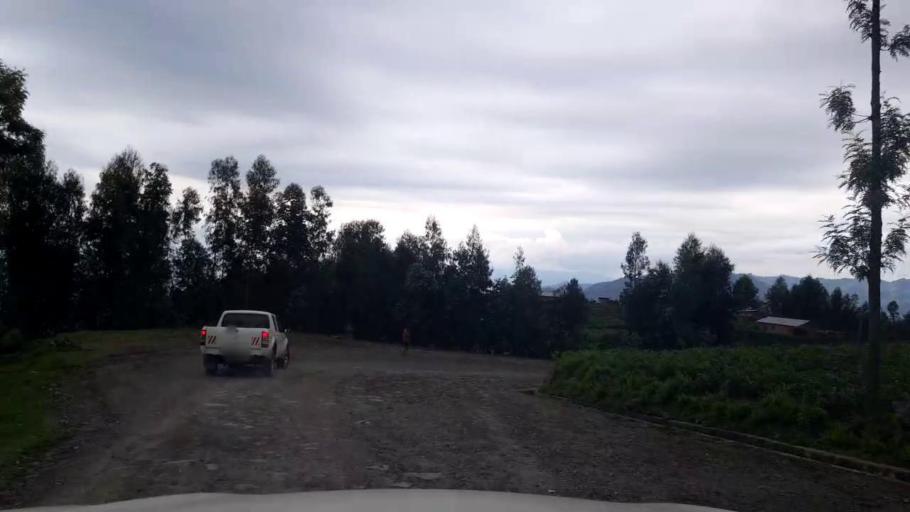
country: RW
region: Northern Province
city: Musanze
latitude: -1.4961
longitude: 29.5328
